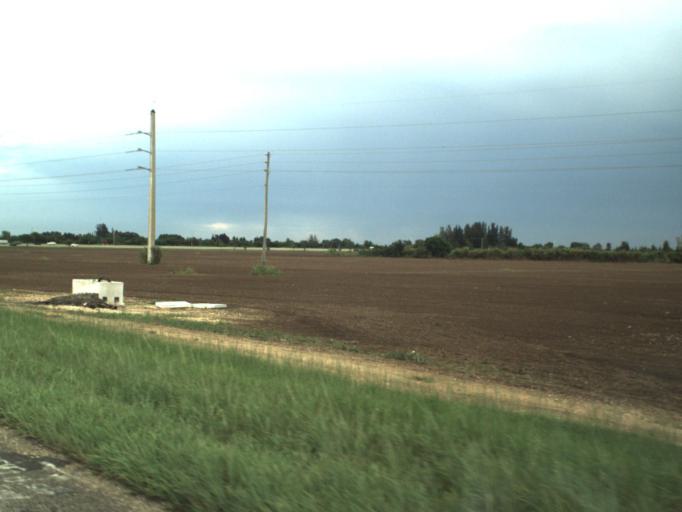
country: US
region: Florida
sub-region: Miami-Dade County
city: The Hammocks
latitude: 25.6836
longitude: -80.4786
